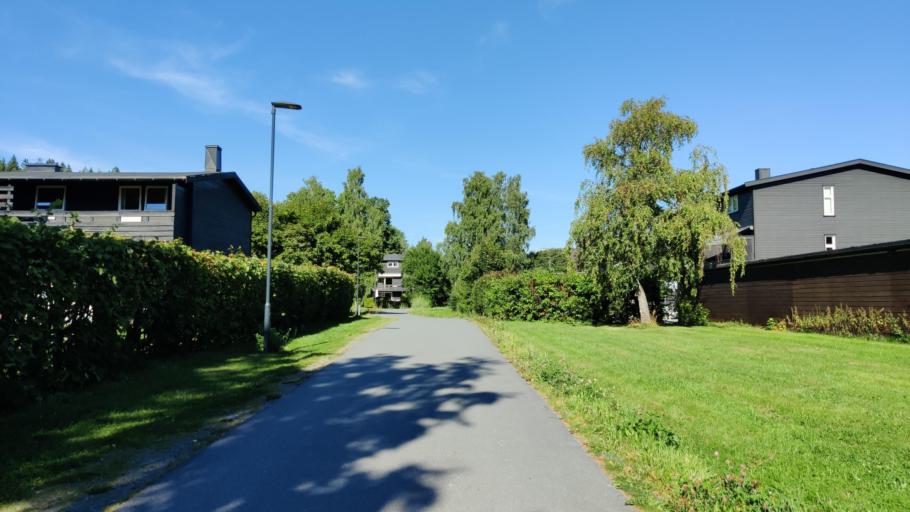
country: NO
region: Akershus
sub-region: Baerum
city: Lysaker
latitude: 59.9312
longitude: 10.6036
